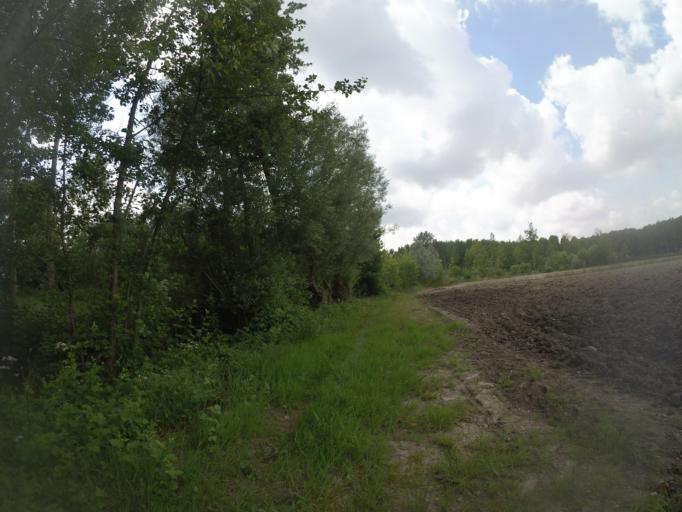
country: IT
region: Friuli Venezia Giulia
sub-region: Provincia di Udine
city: Bertiolo
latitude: 45.9250
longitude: 13.0310
